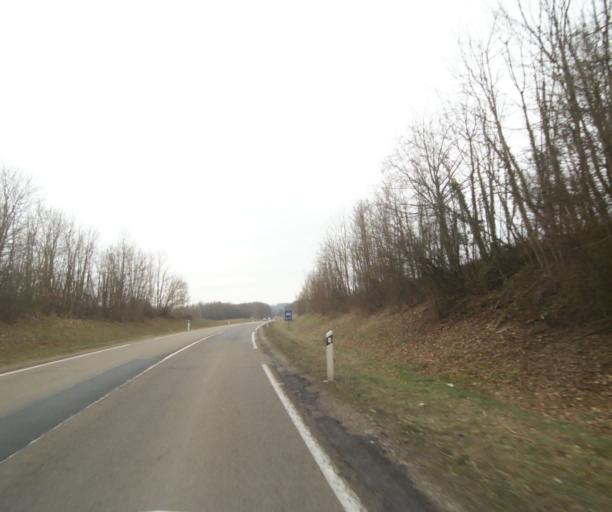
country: FR
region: Champagne-Ardenne
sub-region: Departement de la Haute-Marne
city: Bienville
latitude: 48.5757
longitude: 5.0354
